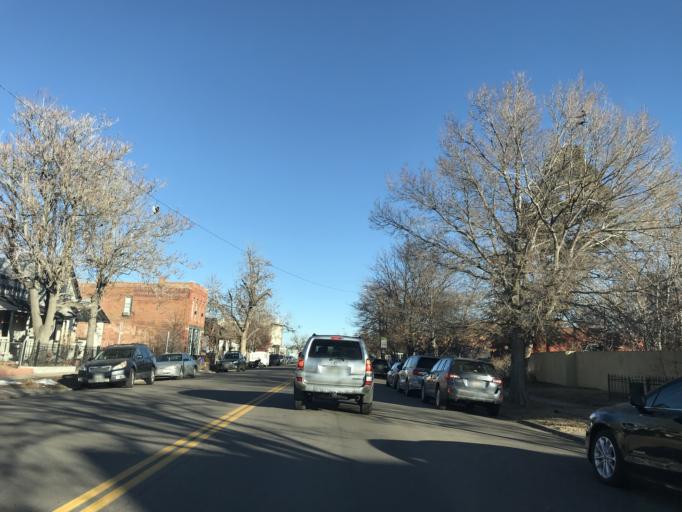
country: US
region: Colorado
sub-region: Denver County
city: Denver
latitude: 39.7684
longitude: -104.9684
